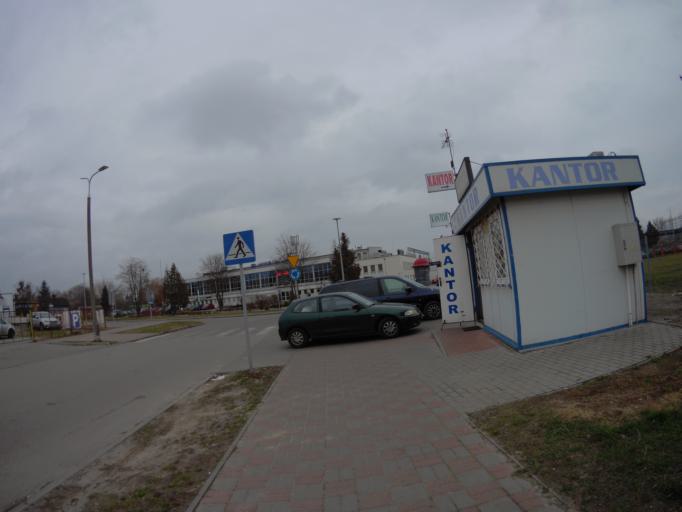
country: PL
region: Lublin Voivodeship
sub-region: Powiat bialski
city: Terespol
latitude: 52.0733
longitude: 23.6040
